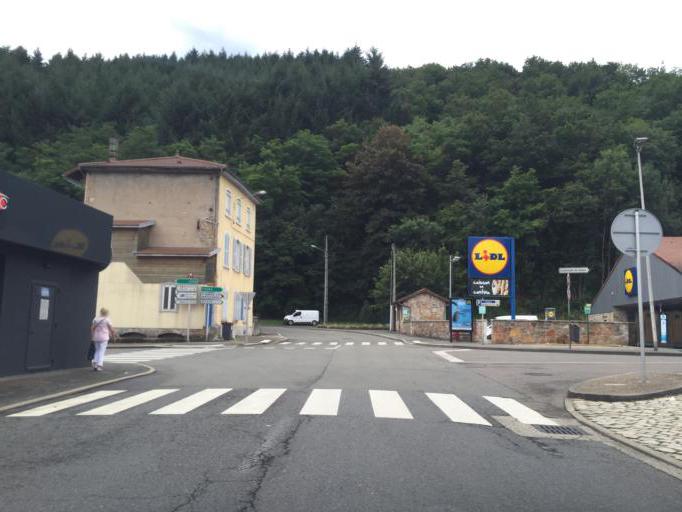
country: FR
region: Rhone-Alpes
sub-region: Departement du Rhone
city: Tarare
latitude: 45.8953
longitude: 4.4290
